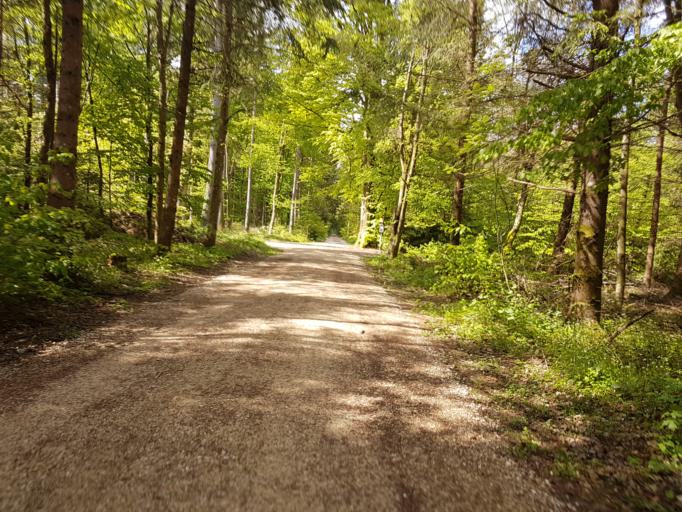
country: CH
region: Aargau
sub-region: Bezirk Zofingen
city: Fulenbach
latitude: 47.2918
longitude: 7.8393
